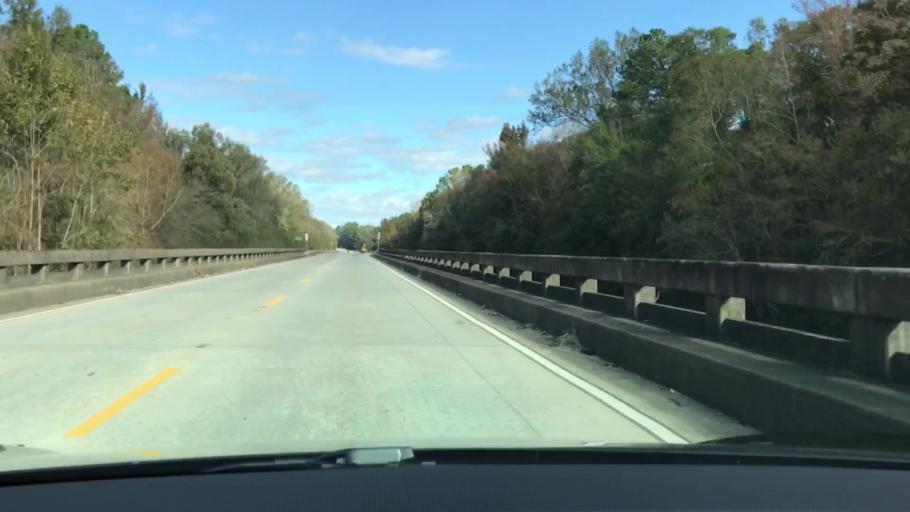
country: US
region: Georgia
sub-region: Jefferson County
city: Louisville
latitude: 32.9679
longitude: -82.3905
